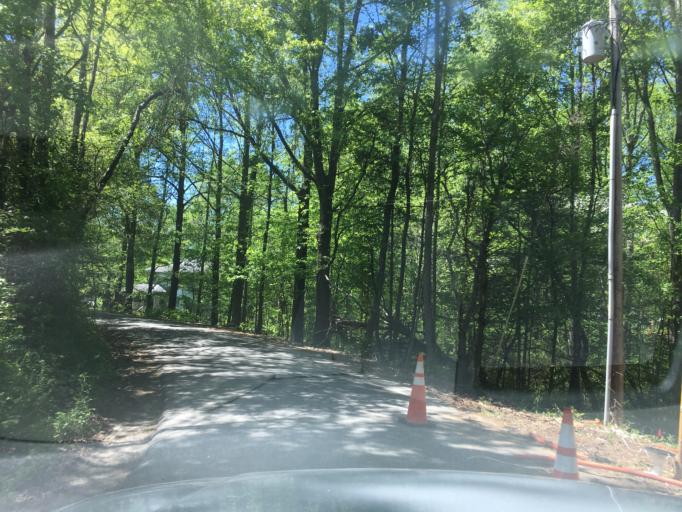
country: US
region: South Carolina
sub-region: Spartanburg County
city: Duncan
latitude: 34.8584
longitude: -82.1595
